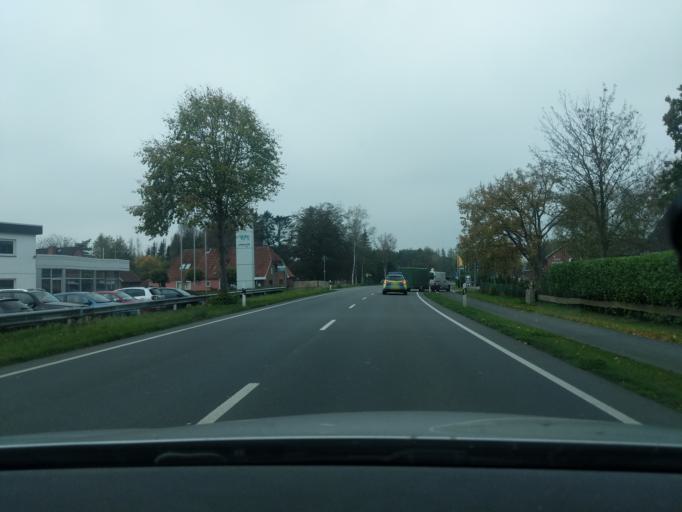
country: DE
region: Lower Saxony
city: Hechthausen
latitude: 53.6522
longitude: 9.2048
